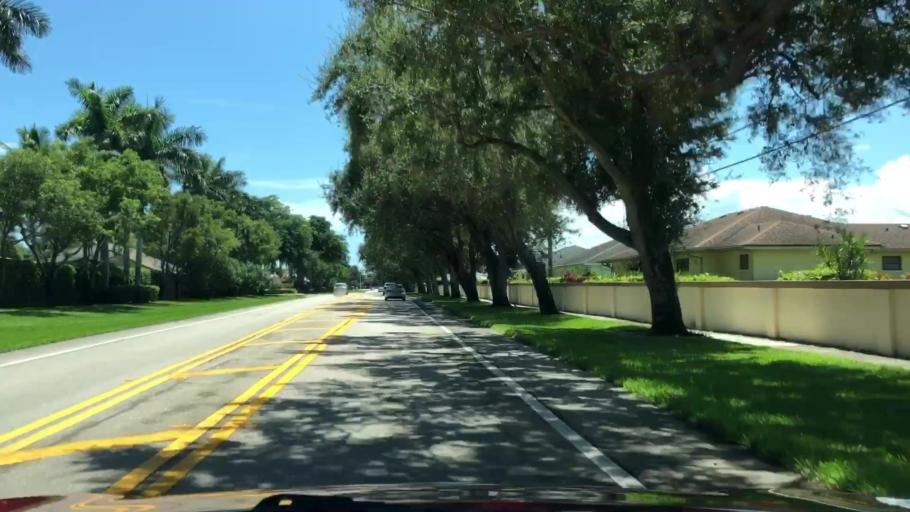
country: US
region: Florida
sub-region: Palm Beach County
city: Boynton Beach
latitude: 26.5185
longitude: -80.1066
